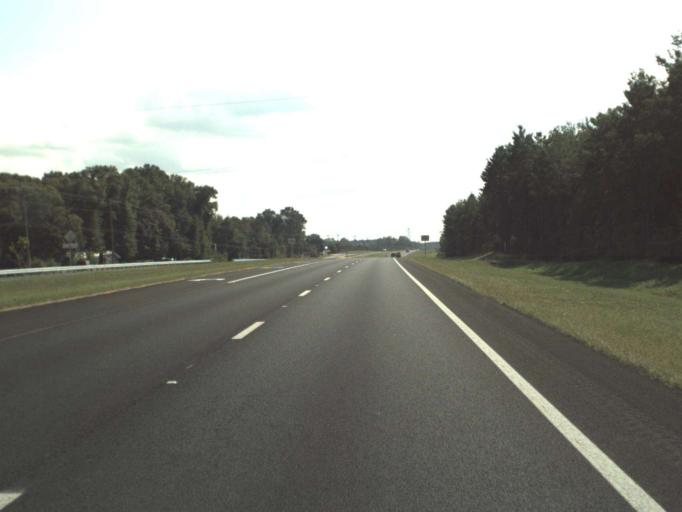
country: US
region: Florida
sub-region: Bay County
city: Laguna Beach
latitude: 30.5036
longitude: -85.8413
